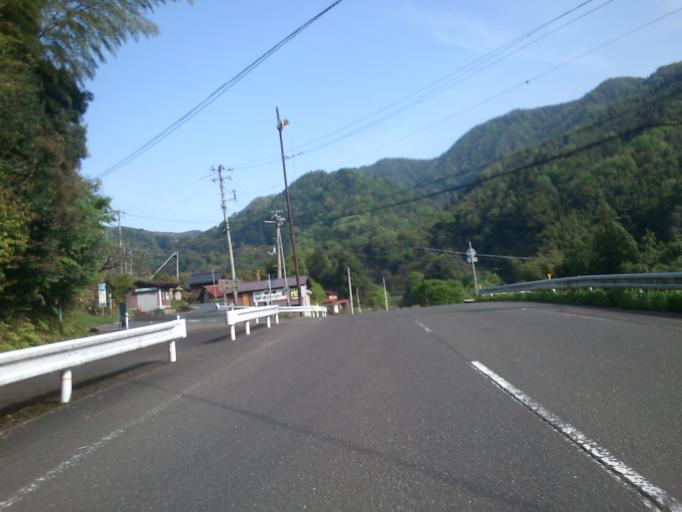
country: JP
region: Kyoto
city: Miyazu
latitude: 35.6302
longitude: 135.2132
